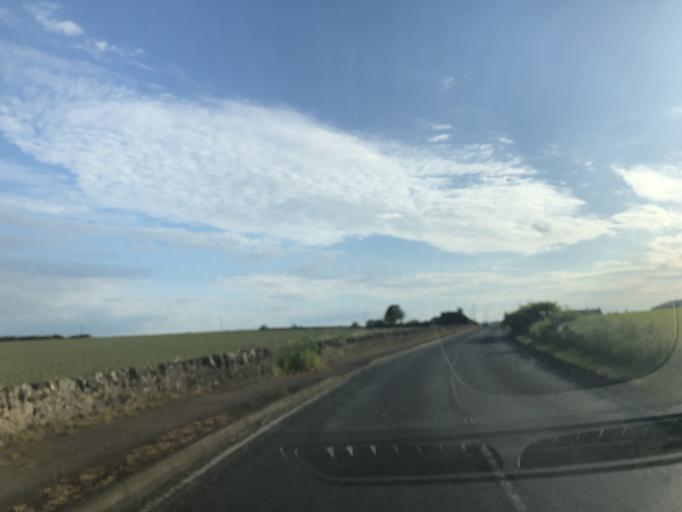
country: GB
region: Scotland
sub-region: Fife
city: Saint Monance
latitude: 56.2056
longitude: -2.7773
